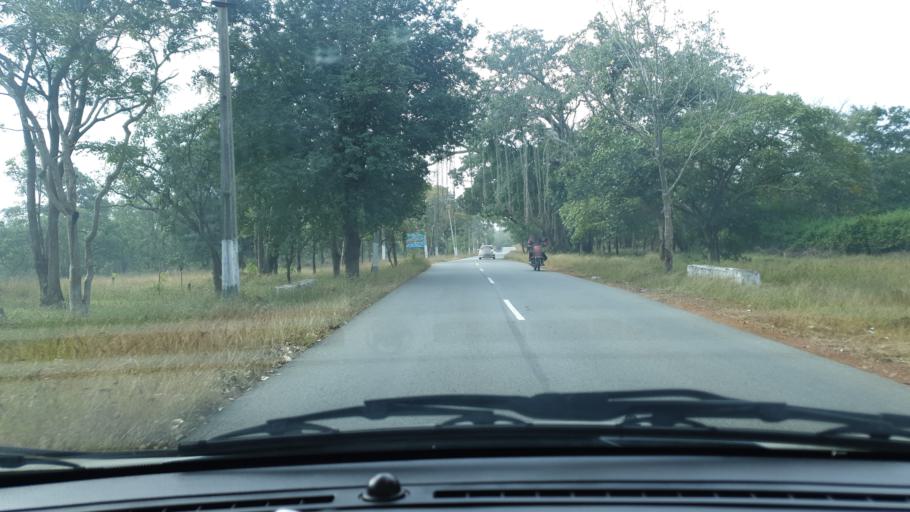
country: IN
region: Andhra Pradesh
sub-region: Kurnool
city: Srisailam
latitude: 16.2828
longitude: 78.7266
